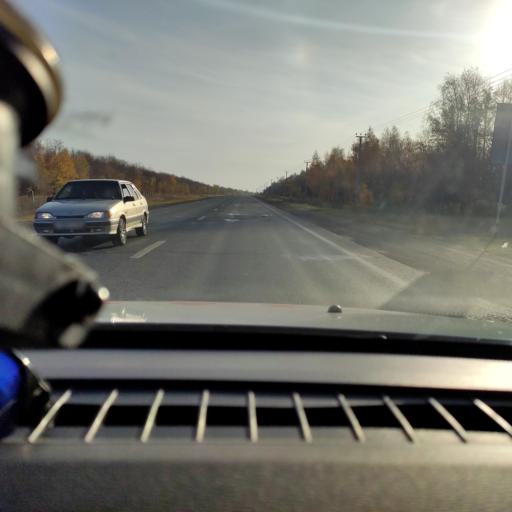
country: RU
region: Samara
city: Chapayevsk
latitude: 52.9969
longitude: 49.7933
